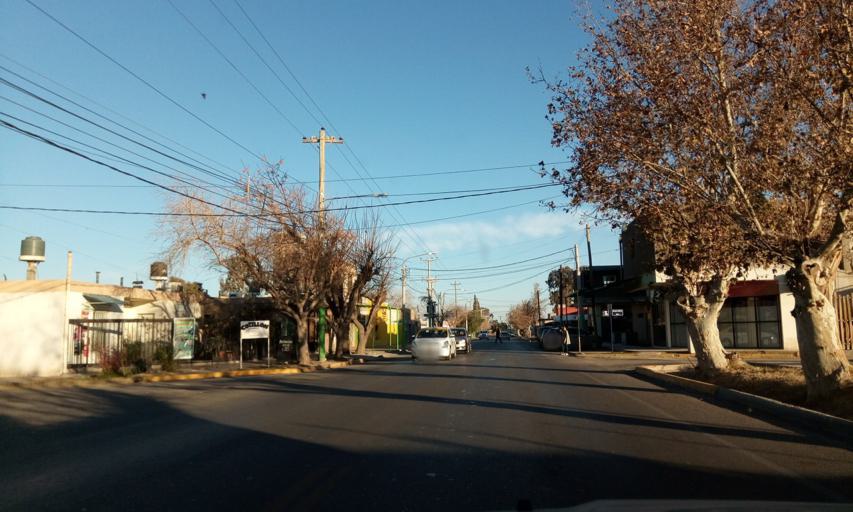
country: AR
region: San Juan
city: San Juan
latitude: -31.5357
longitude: -68.5930
